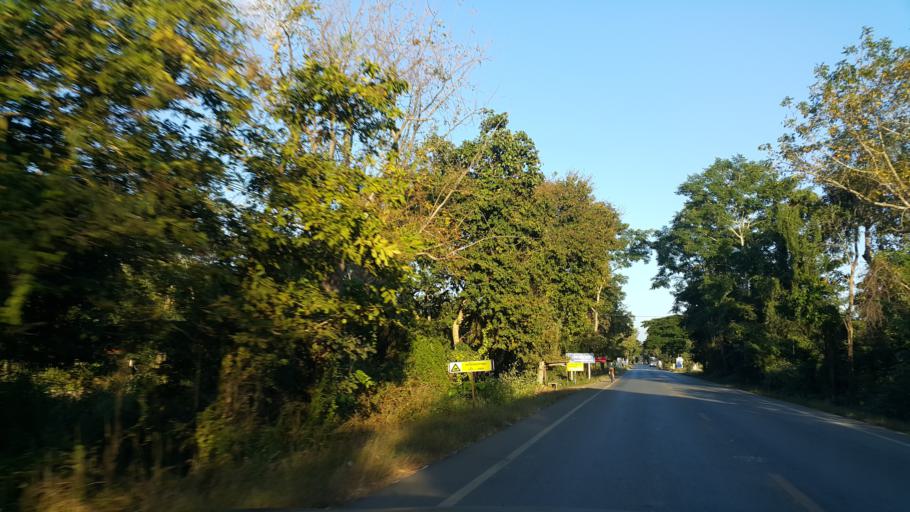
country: TH
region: Sukhothai
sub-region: Amphoe Si Satchanalai
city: Si Satchanalai
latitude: 17.5470
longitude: 99.8456
